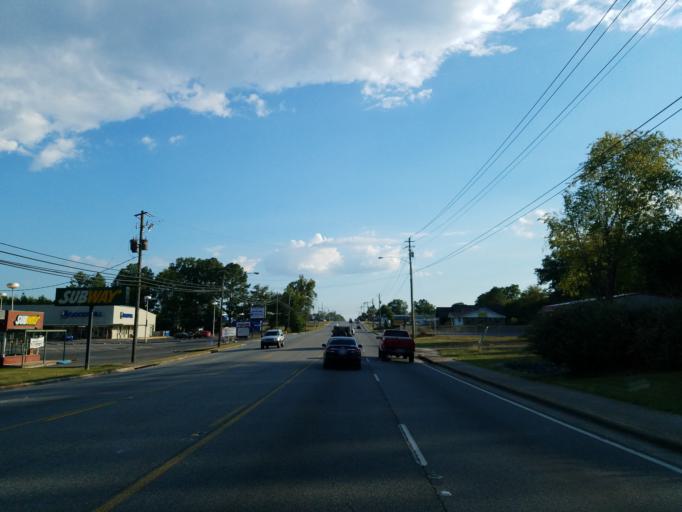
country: US
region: Georgia
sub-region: Murray County
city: Chatsworth
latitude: 34.7795
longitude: -84.7697
